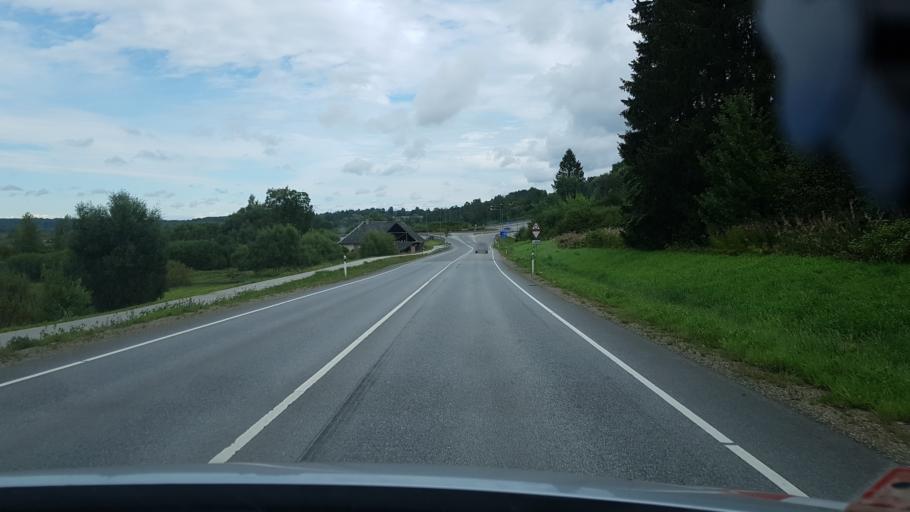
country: EE
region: Viljandimaa
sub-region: Viiratsi vald
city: Viiratsi
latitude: 58.3605
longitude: 25.6315
